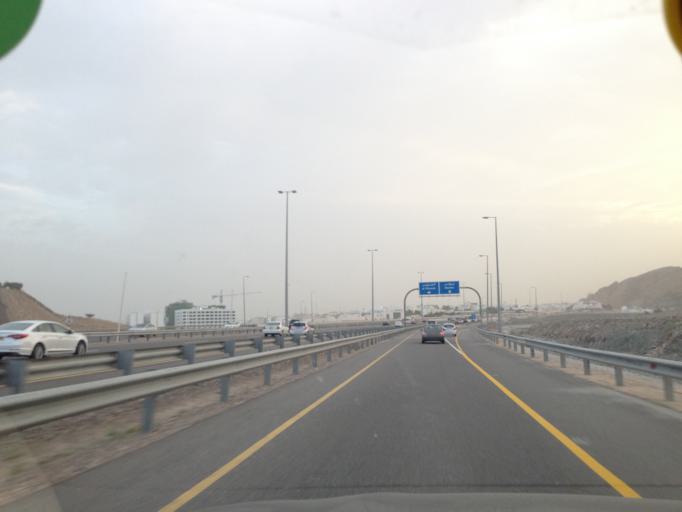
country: OM
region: Muhafazat Masqat
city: Bawshar
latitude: 23.5799
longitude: 58.4419
